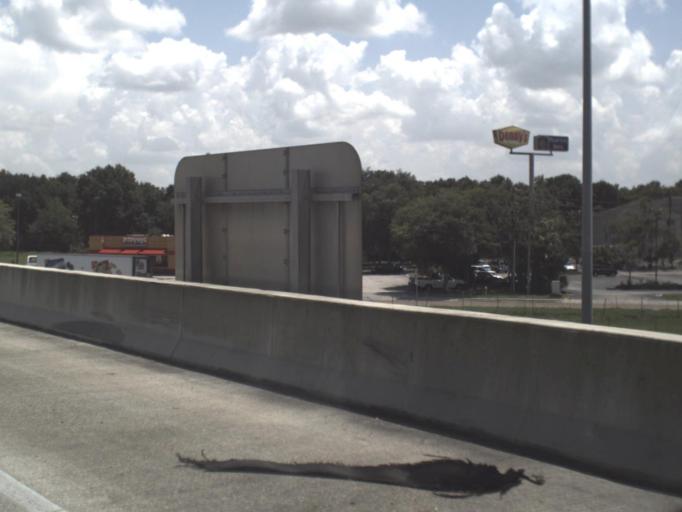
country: US
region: Florida
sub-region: Hillsborough County
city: Plant City
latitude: 28.0365
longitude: -82.1045
